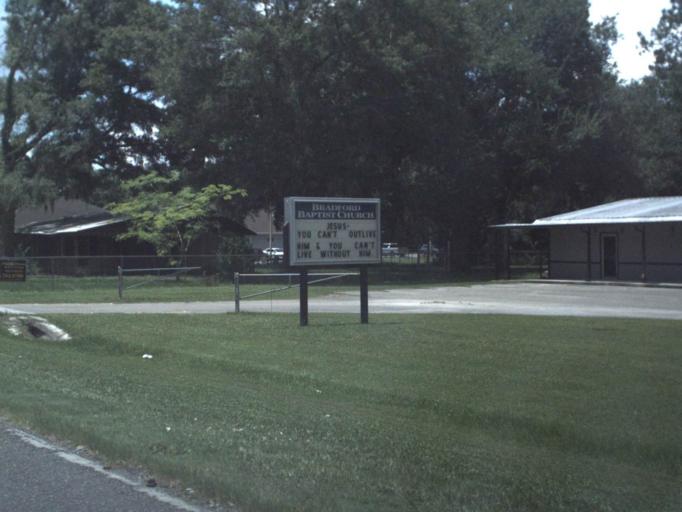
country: US
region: Florida
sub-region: Bradford County
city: Starke
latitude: 29.9285
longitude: -82.1014
